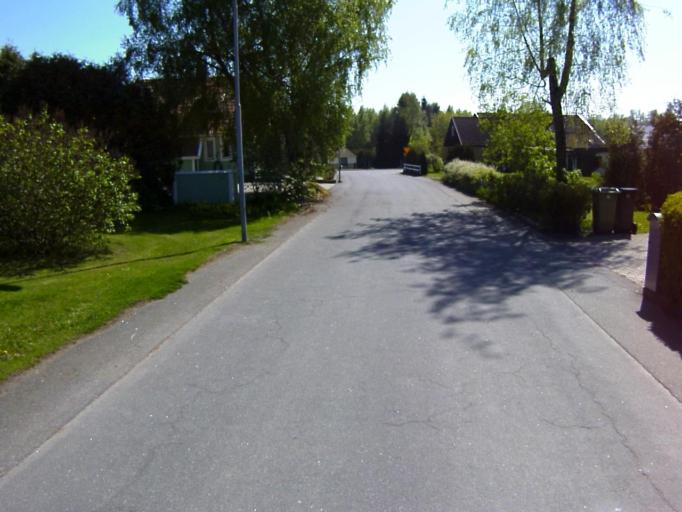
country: SE
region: Skane
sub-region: Kristianstads Kommun
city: Degeberga
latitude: 55.8992
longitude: 14.1008
